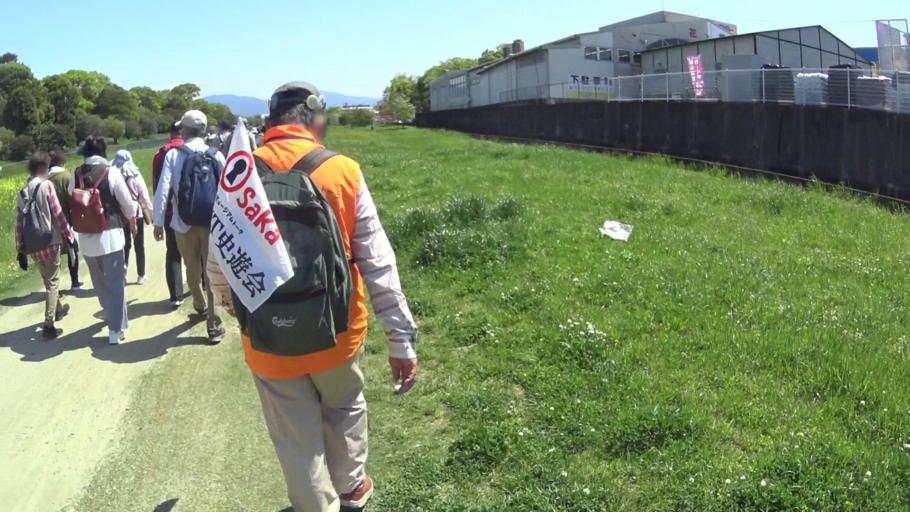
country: JP
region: Osaka
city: Kashihara
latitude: 34.5637
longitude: 135.6054
